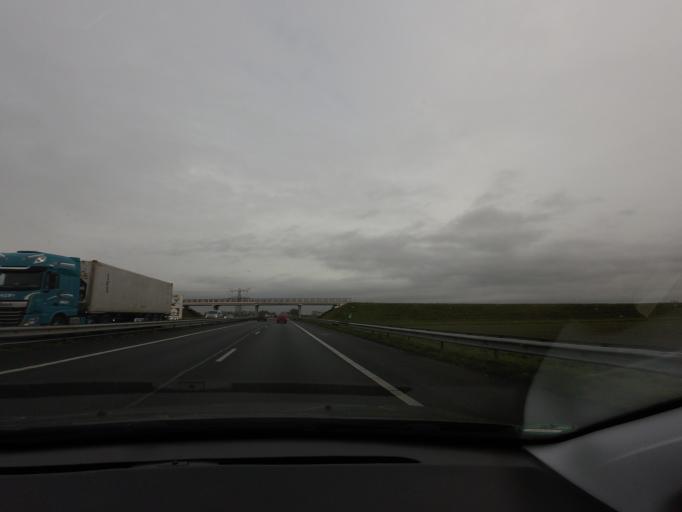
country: NL
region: South Holland
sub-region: Gemeente Binnenmaas
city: Mijnsheerenland
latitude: 51.7970
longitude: 4.4492
